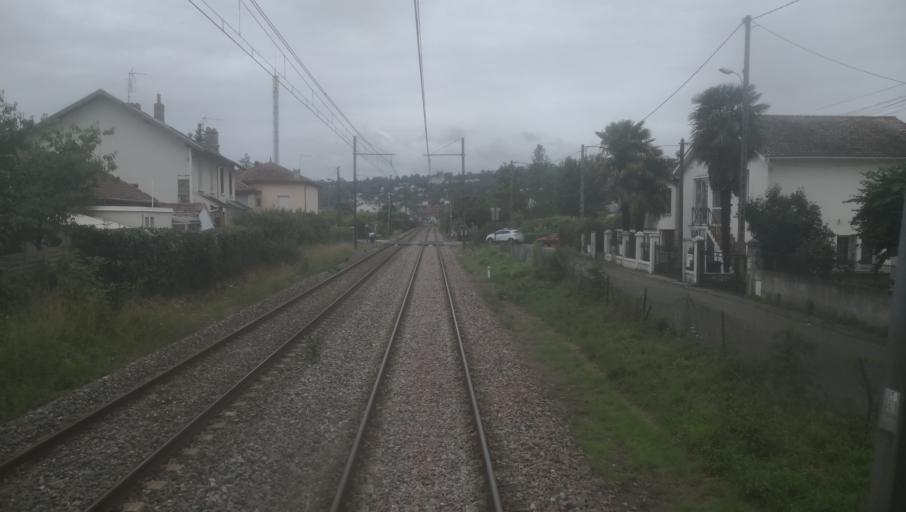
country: FR
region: Aquitaine
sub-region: Departement du Lot-et-Garonne
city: Agen
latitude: 44.2028
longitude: 0.6367
